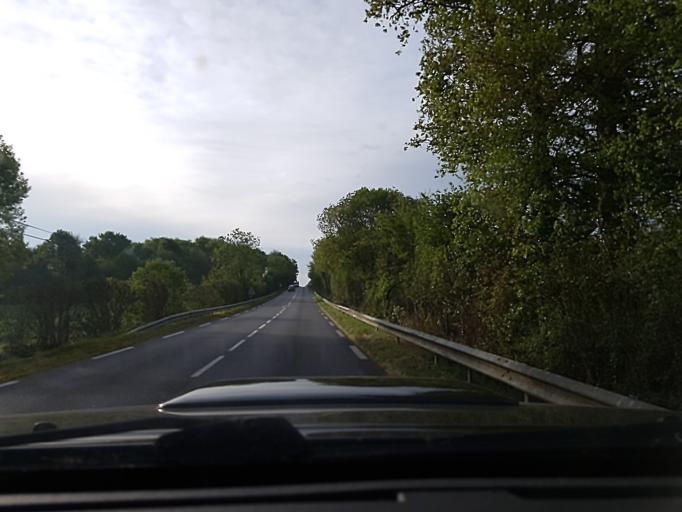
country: FR
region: Pays de la Loire
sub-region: Departement de la Vendee
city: Aizenay
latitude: 46.7550
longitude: -1.6370
